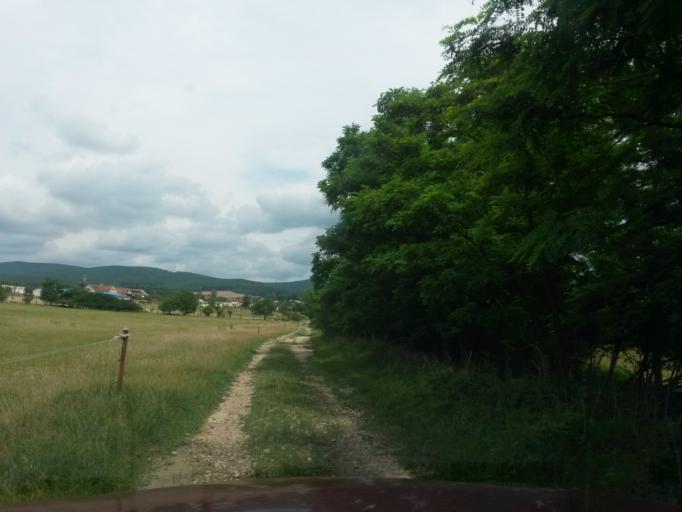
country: SK
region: Kosicky
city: Moldava nad Bodvou
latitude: 48.6665
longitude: 21.1123
